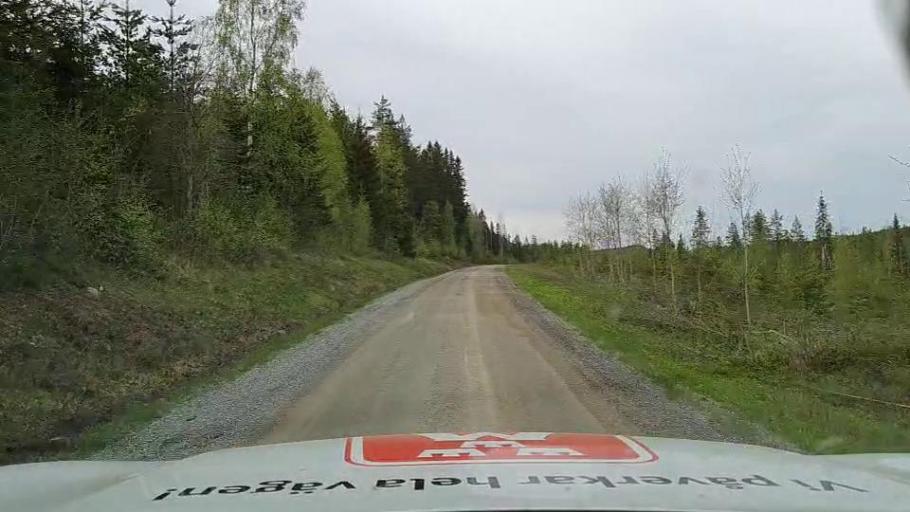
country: SE
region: Jaemtland
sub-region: Bergs Kommun
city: Hoverberg
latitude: 62.5459
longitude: 14.8986
